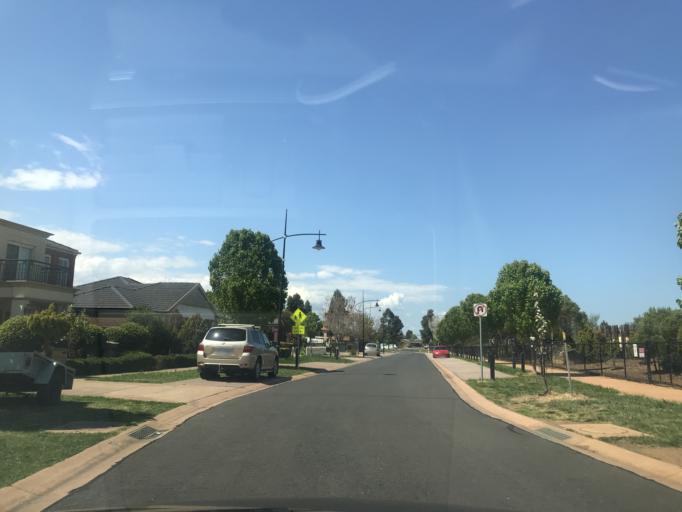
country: AU
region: Victoria
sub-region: Wyndham
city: Hoppers Crossing
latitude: -37.8899
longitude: 144.7268
